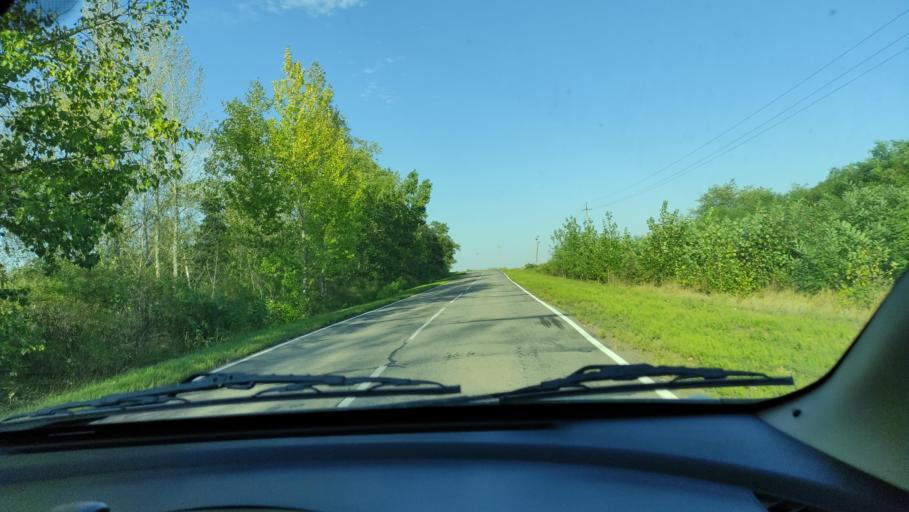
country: RU
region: Voronezj
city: Verkhniy Mamon
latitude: 50.1227
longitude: 40.3076
